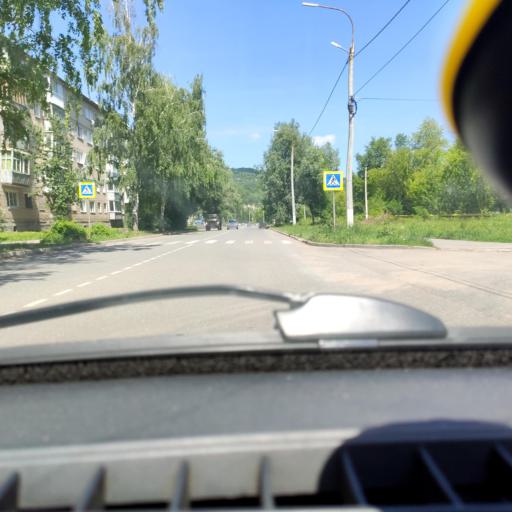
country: RU
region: Samara
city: Zhigulevsk
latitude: 53.4013
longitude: 49.5106
